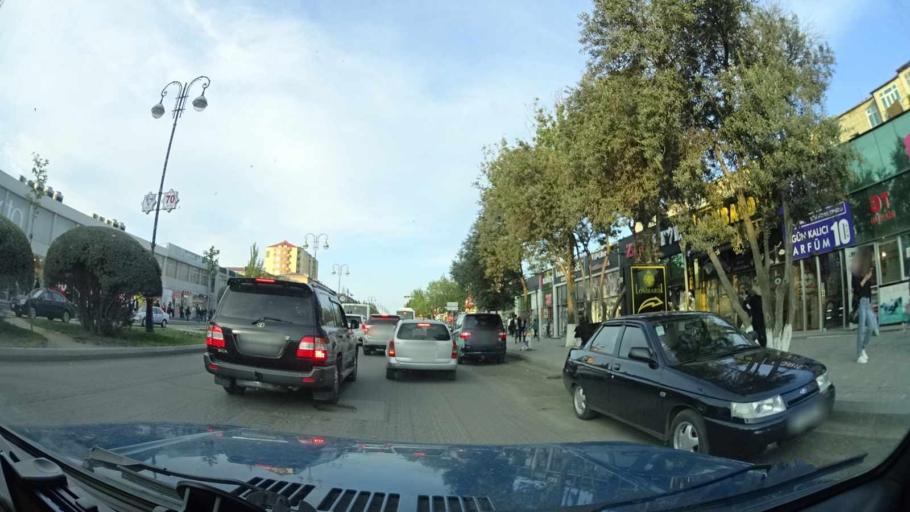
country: AZ
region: Sumqayit
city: Sumqayit
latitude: 40.5891
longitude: 49.6750
